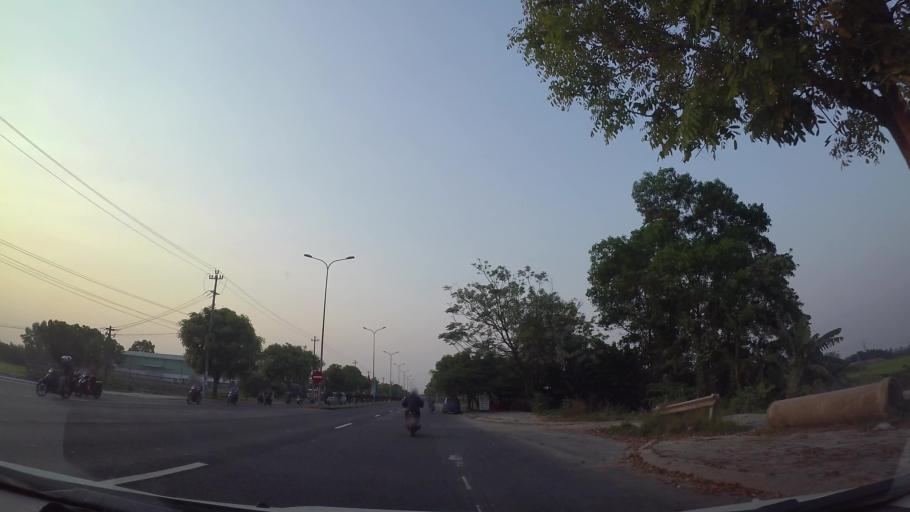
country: VN
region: Da Nang
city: Cam Le
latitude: 15.9641
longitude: 108.2123
